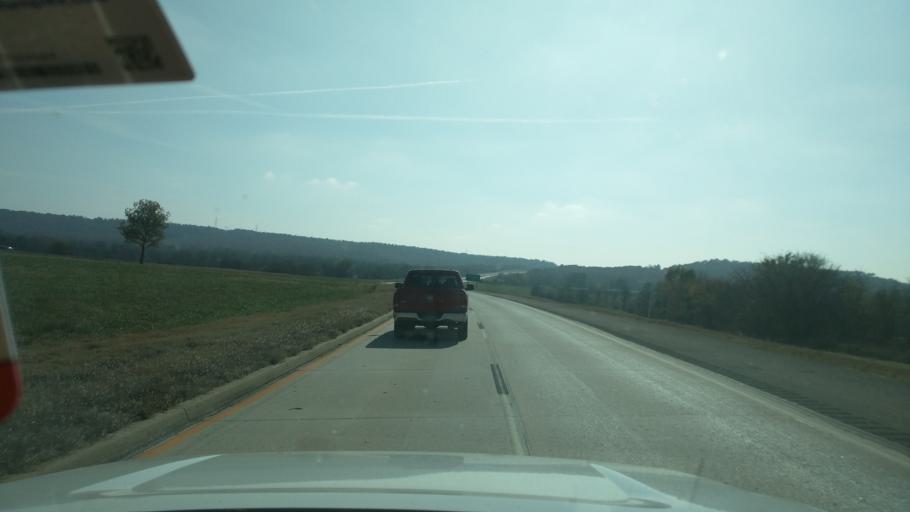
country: US
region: Oklahoma
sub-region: Muskogee County
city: Muskogee
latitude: 35.6778
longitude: -95.3106
